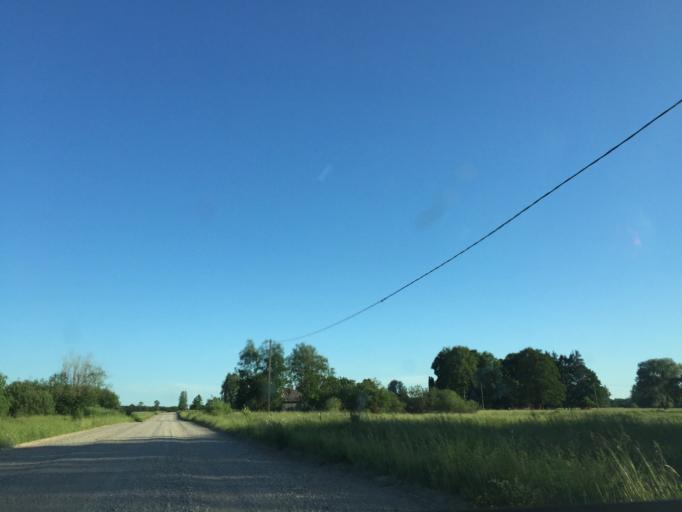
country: LV
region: Broceni
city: Broceni
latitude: 56.8174
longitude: 22.5463
